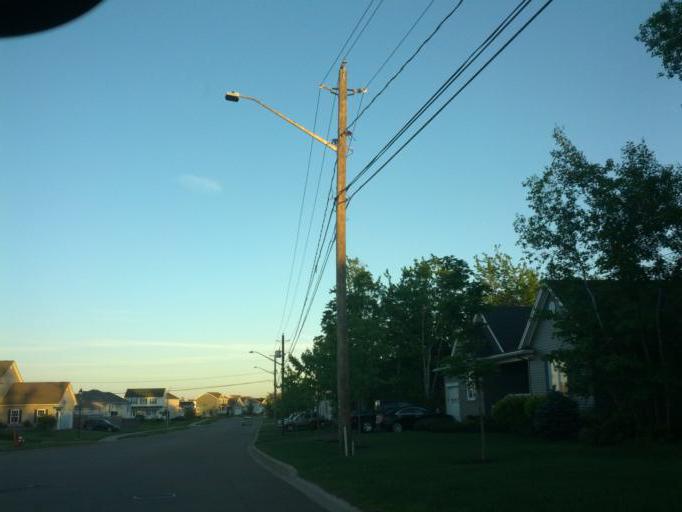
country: CA
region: New Brunswick
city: Moncton
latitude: 46.1126
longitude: -64.8650
